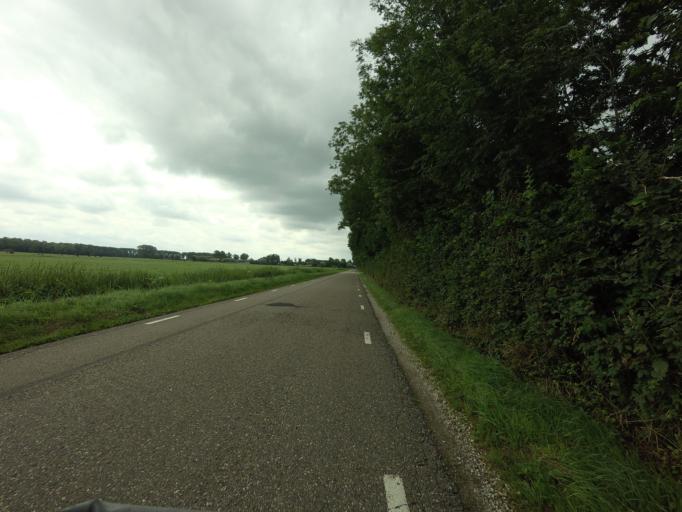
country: NL
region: South Holland
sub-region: Gemeente Giessenlanden
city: Giessenburg
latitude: 51.8957
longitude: 4.9024
